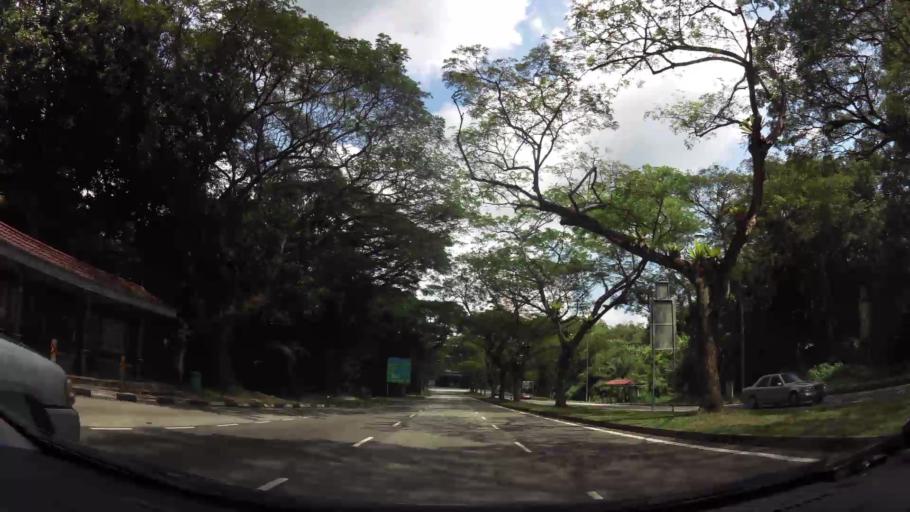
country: MY
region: Johor
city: Johor Bahru
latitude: 1.3917
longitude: 103.8183
